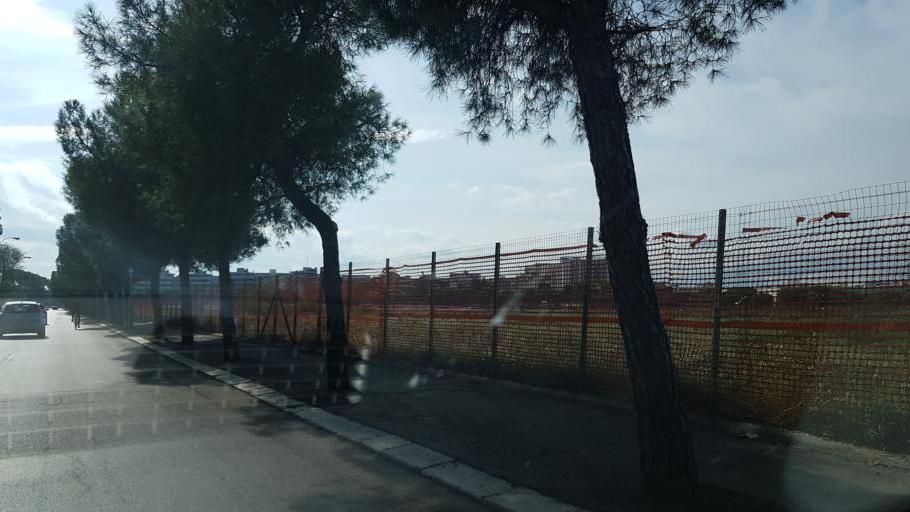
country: IT
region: Apulia
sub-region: Provincia di Foggia
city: Foggia
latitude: 41.4596
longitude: 15.5643
